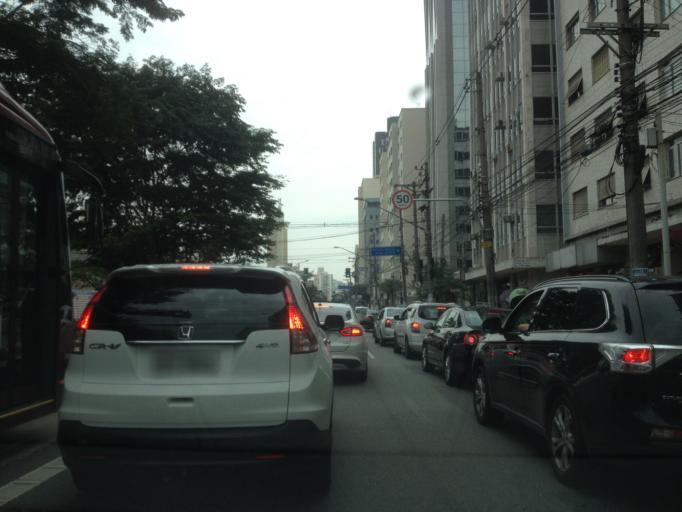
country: BR
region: Sao Paulo
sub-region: Sao Paulo
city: Sao Paulo
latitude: -23.5783
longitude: -46.6711
